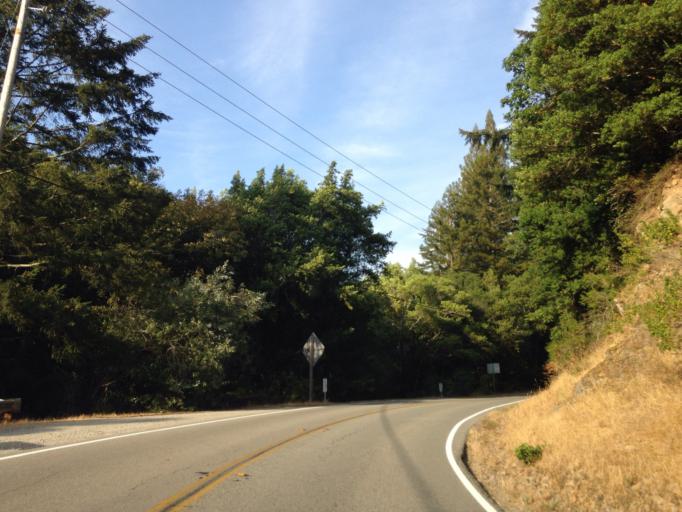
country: US
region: California
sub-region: Marin County
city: Woodacre
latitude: 38.0442
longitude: -122.6329
